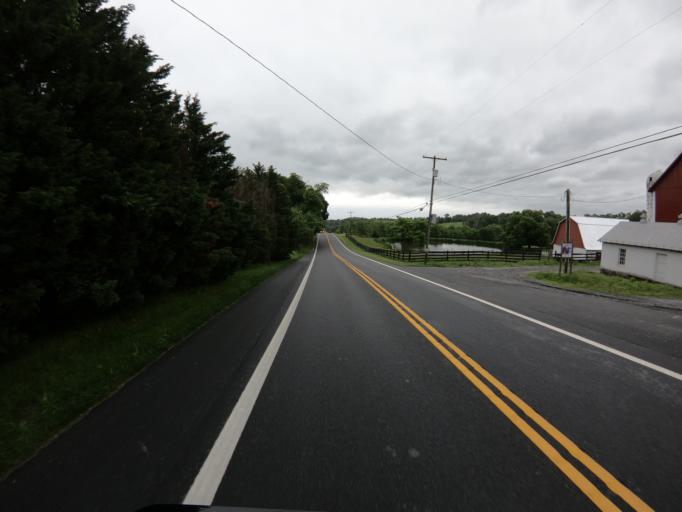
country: US
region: Maryland
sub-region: Frederick County
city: Myersville
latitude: 39.4717
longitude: -77.6009
